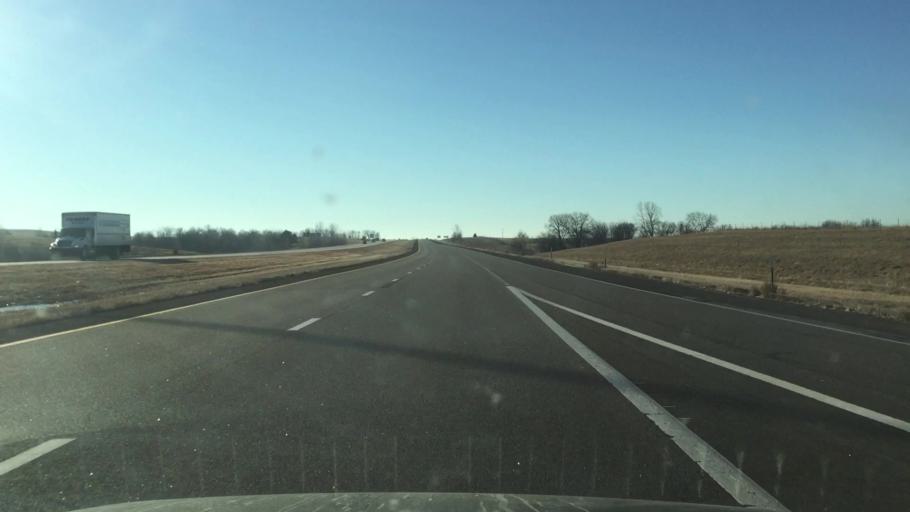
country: US
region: Kansas
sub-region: Miami County
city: Paola
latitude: 38.6187
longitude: -94.8363
